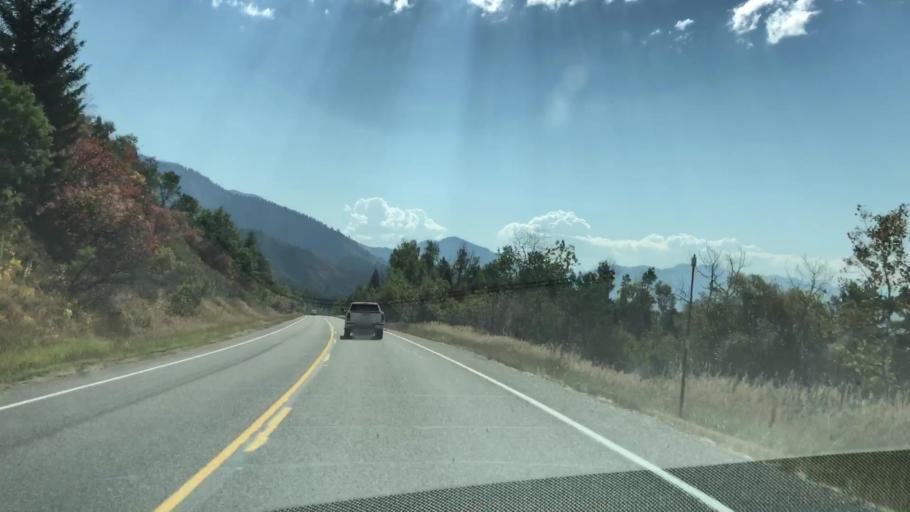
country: US
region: Wyoming
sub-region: Teton County
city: Hoback
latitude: 43.2277
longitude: -111.0860
